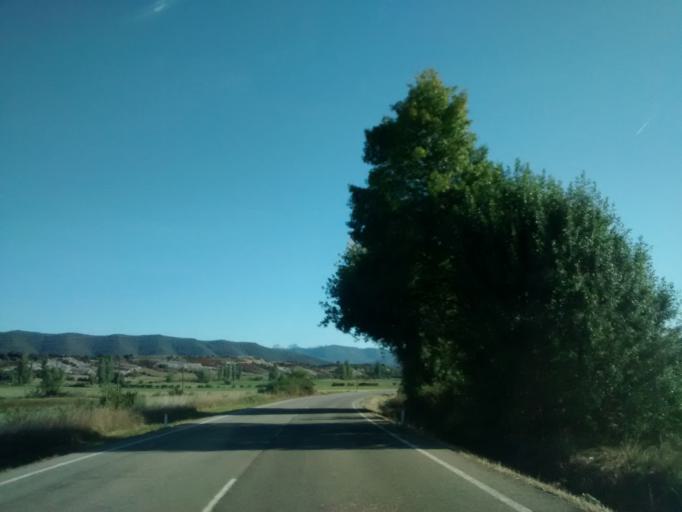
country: ES
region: Aragon
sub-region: Provincia de Huesca
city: Bailo
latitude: 42.5700
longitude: -0.7717
